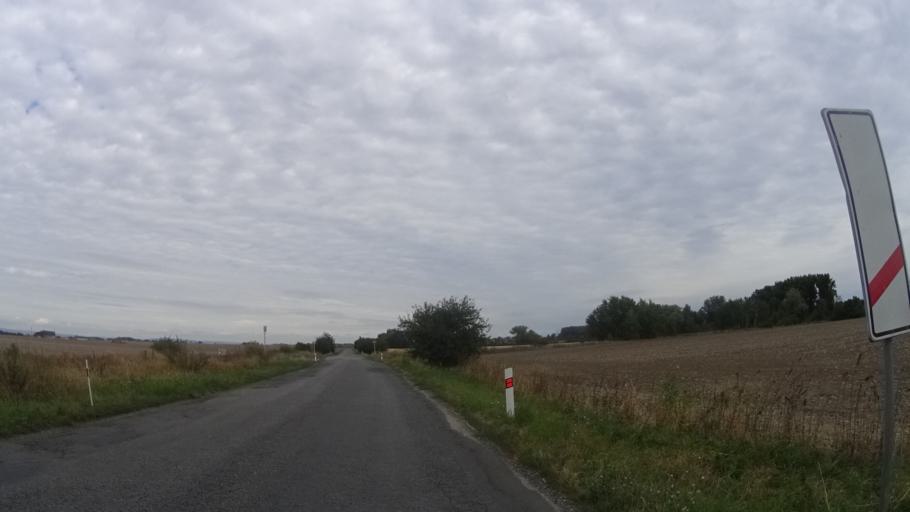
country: CZ
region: Olomoucky
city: Tovacov
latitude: 49.4042
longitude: 17.2865
